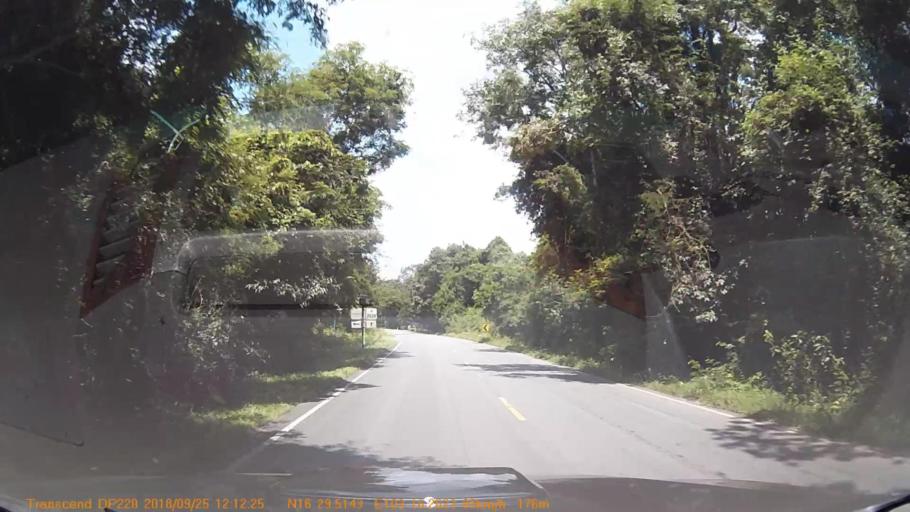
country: TH
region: Kalasin
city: Huai Mek
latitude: 16.4920
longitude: 103.2711
